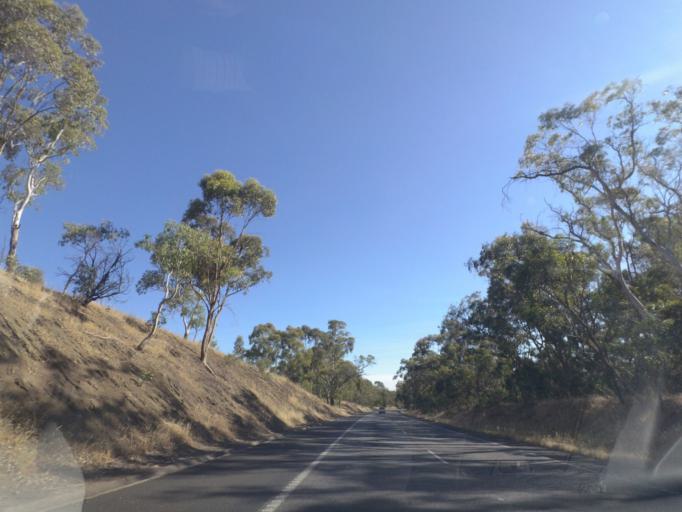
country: AU
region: Victoria
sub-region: Murrindindi
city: Kinglake West
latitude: -37.1692
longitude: 145.0770
